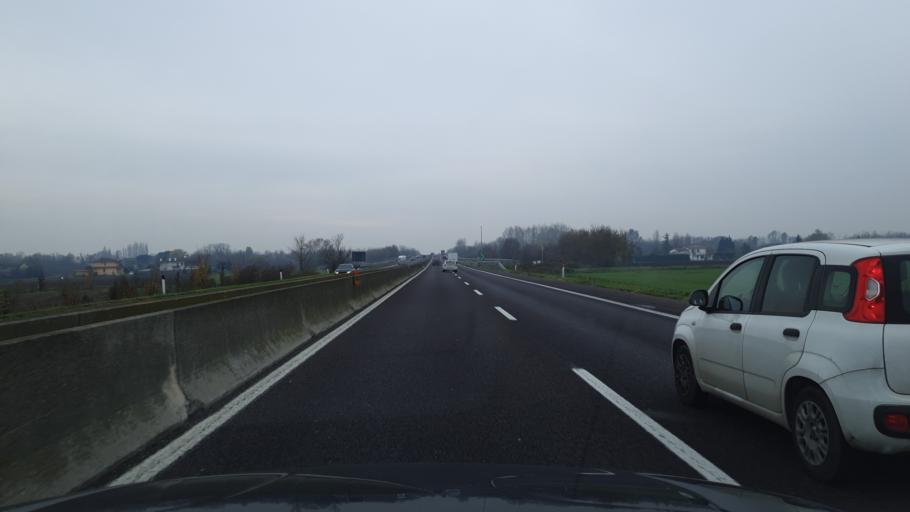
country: IT
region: Veneto
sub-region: Provincia di Rovigo
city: Villamarzana
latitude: 45.0109
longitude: 11.6835
